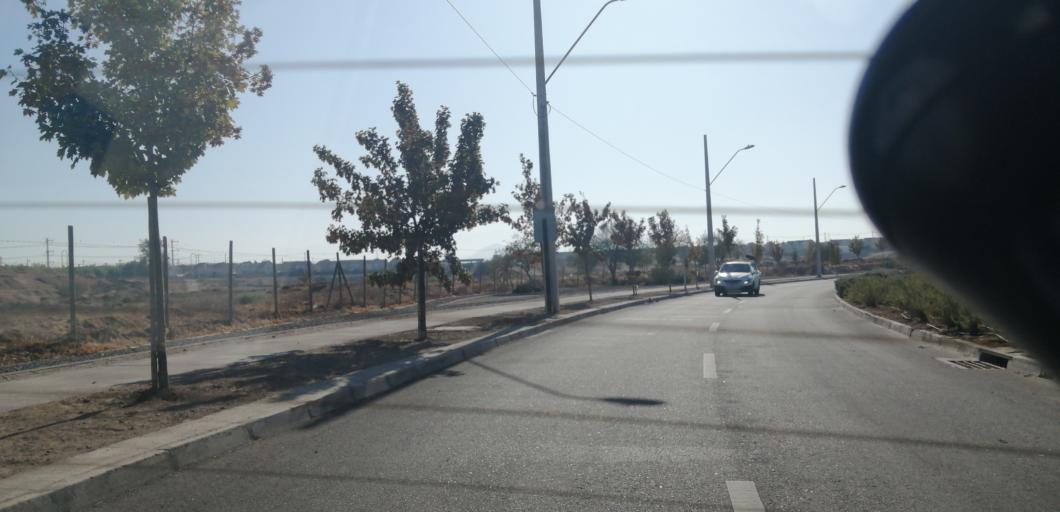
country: CL
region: Santiago Metropolitan
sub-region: Provincia de Santiago
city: Lo Prado
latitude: -33.4369
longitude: -70.7832
